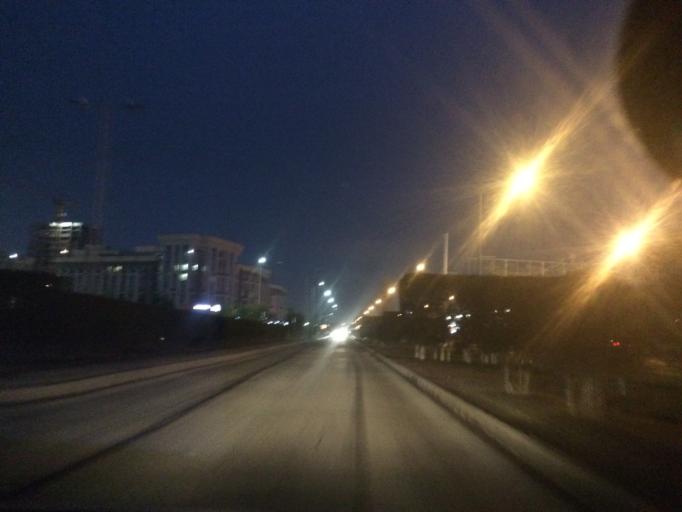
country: KZ
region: Astana Qalasy
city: Astana
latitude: 51.1391
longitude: 71.4171
